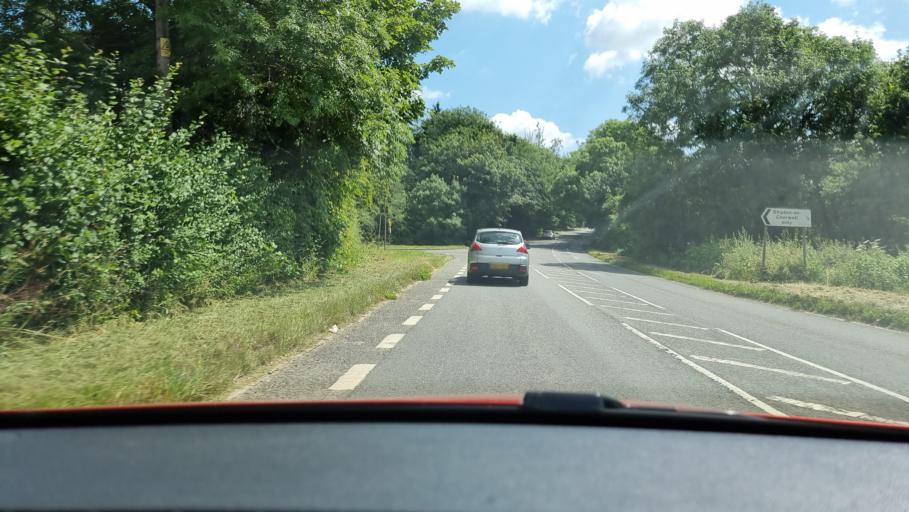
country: GB
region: England
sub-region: Oxfordshire
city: Kidlington
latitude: 51.8474
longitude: -1.3118
